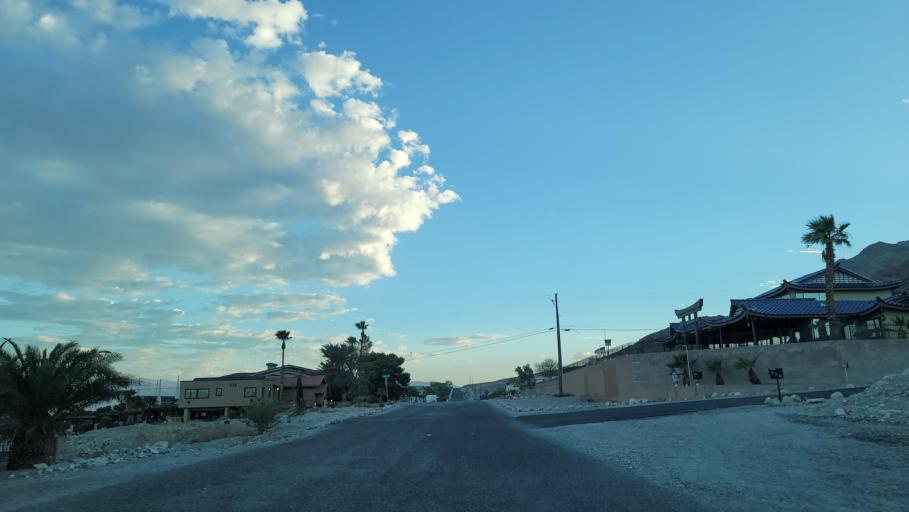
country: US
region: Nevada
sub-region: Clark County
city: Sunrise Manor
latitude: 36.1685
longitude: -115.0168
